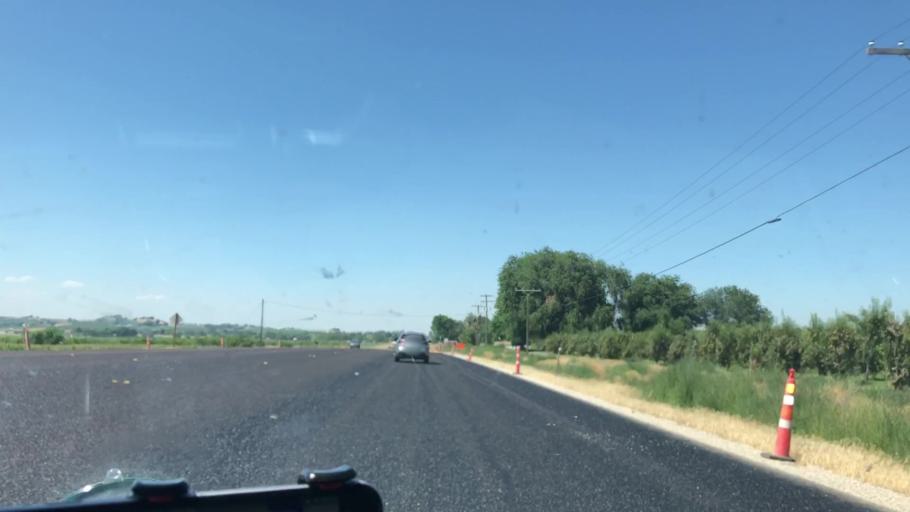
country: US
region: Idaho
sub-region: Owyhee County
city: Marsing
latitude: 43.5690
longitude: -116.7924
